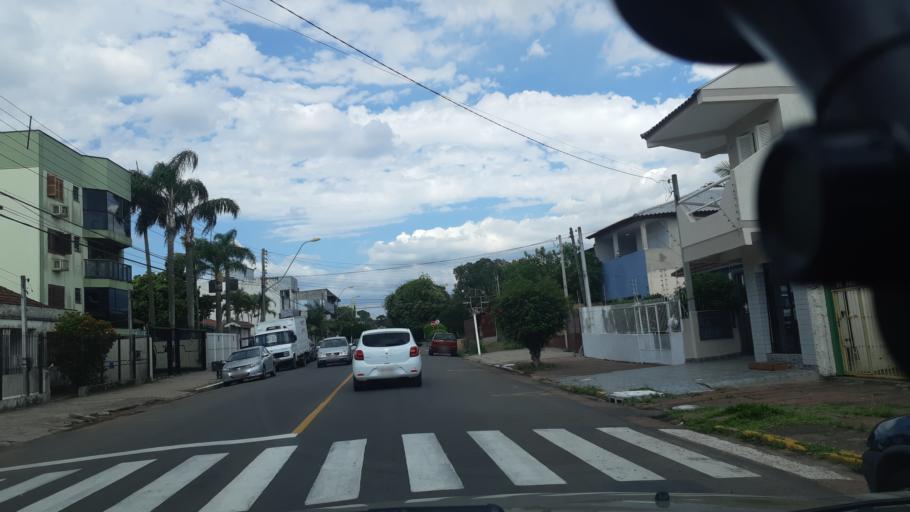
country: BR
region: Rio Grande do Sul
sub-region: Esteio
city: Esteio
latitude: -29.8503
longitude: -51.1721
